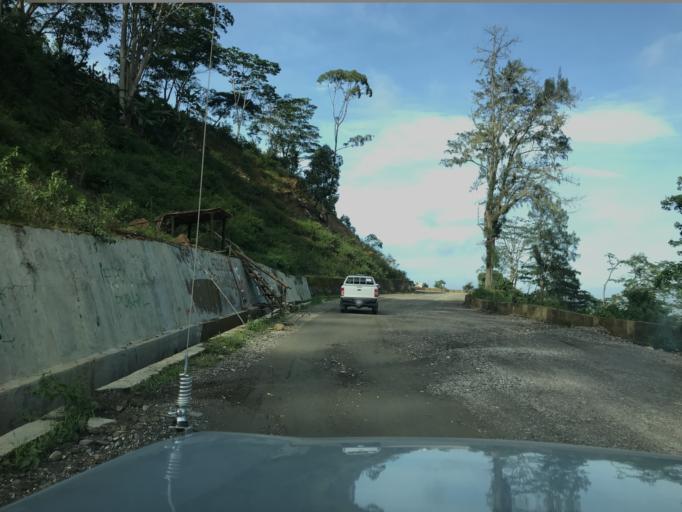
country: TL
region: Aileu
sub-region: Aileu Villa
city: Aileu
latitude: -8.6725
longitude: 125.5511
